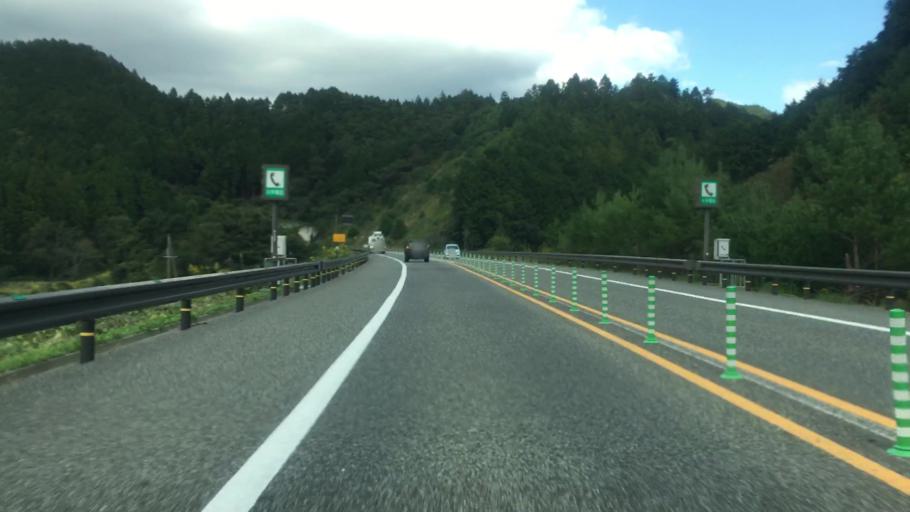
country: JP
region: Kyoto
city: Fukuchiyama
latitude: 35.2576
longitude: 135.0127
